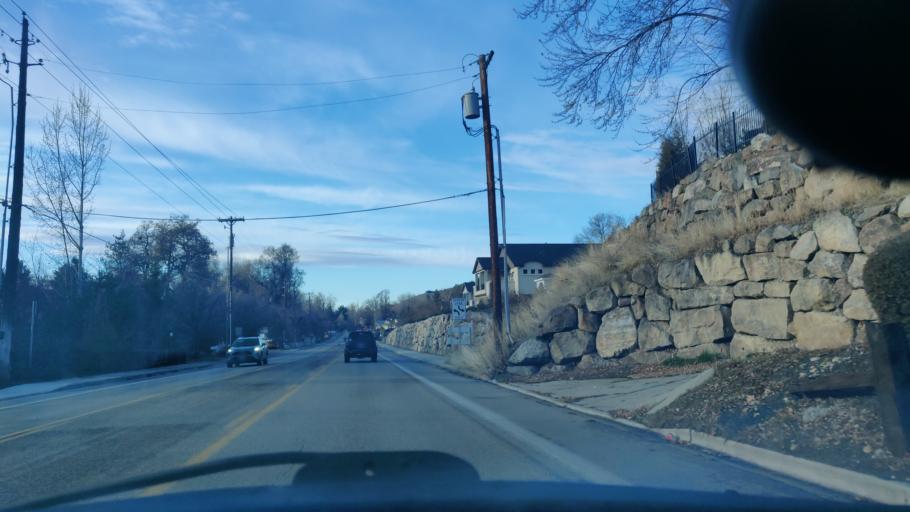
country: US
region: Idaho
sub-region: Ada County
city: Garden City
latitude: 43.6438
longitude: -116.2150
